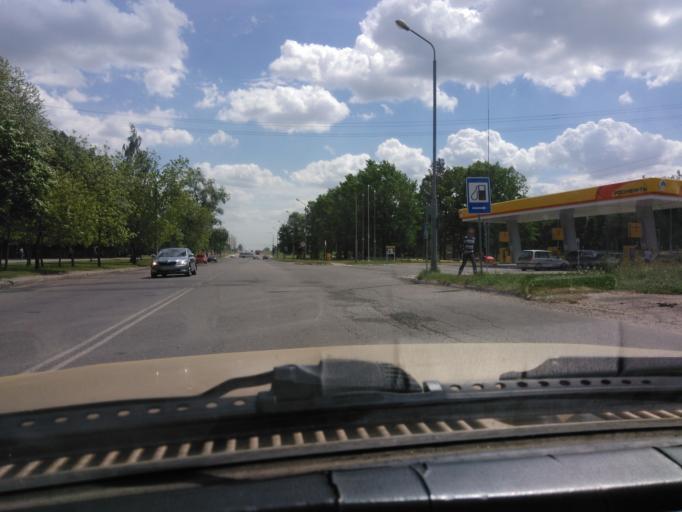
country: BY
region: Mogilev
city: Mahilyow
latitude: 53.9477
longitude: 30.3534
